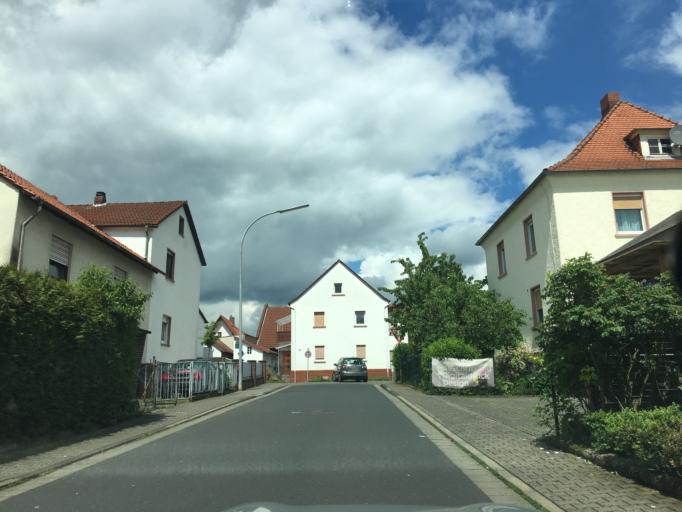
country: DE
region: Hesse
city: Hain-Grundau
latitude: 50.1997
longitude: 9.1131
